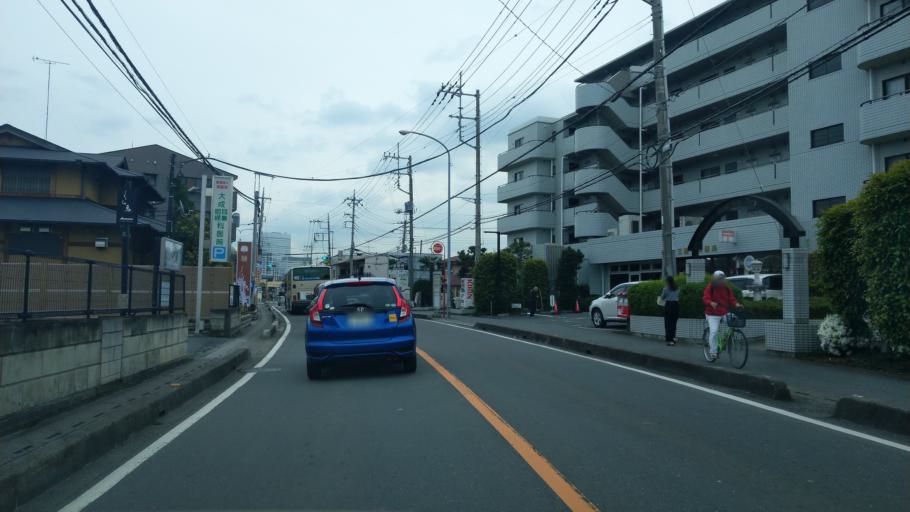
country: JP
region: Saitama
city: Yono
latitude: 35.9070
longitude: 139.6030
